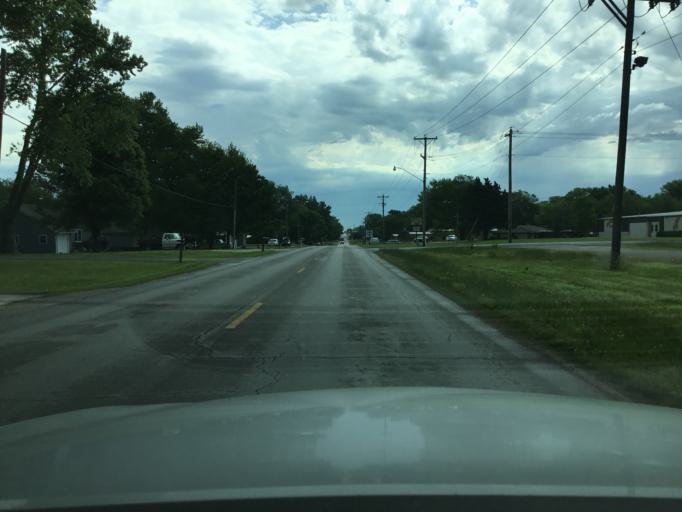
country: US
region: Kansas
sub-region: Montgomery County
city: Coffeyville
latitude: 37.0364
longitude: -95.6542
